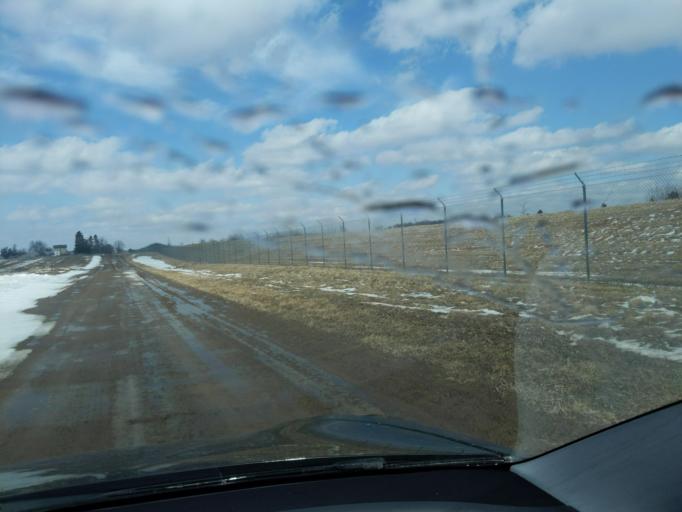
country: US
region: Michigan
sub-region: Livingston County
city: Fowlerville
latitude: 42.6208
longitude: -84.0617
